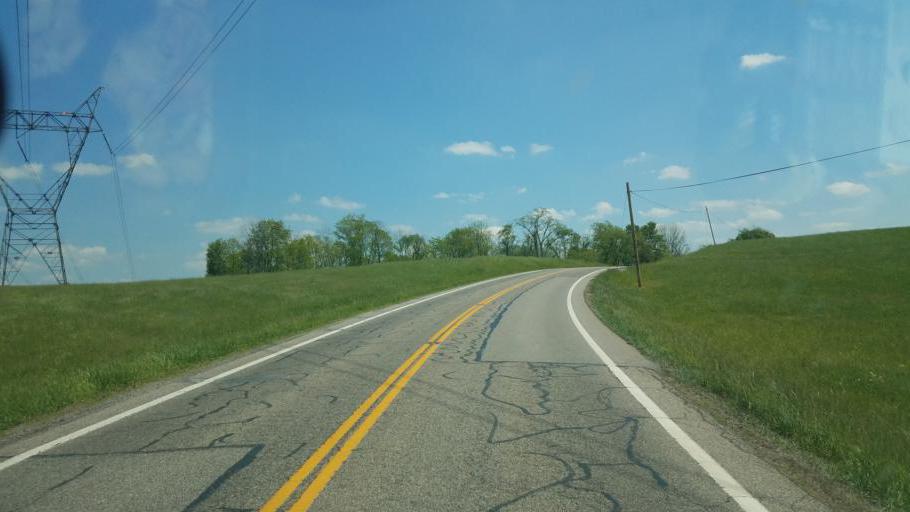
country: US
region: Ohio
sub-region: Muskingum County
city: Frazeysburg
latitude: 40.2117
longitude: -82.2513
